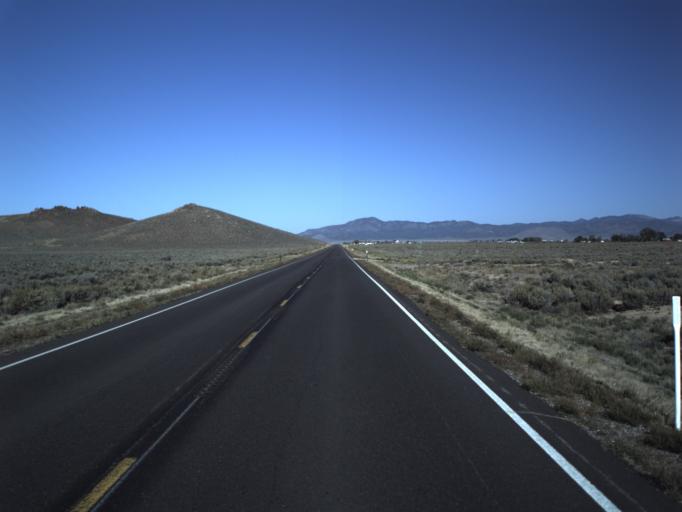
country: US
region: Utah
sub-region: Washington County
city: Enterprise
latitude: 37.7385
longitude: -113.7371
